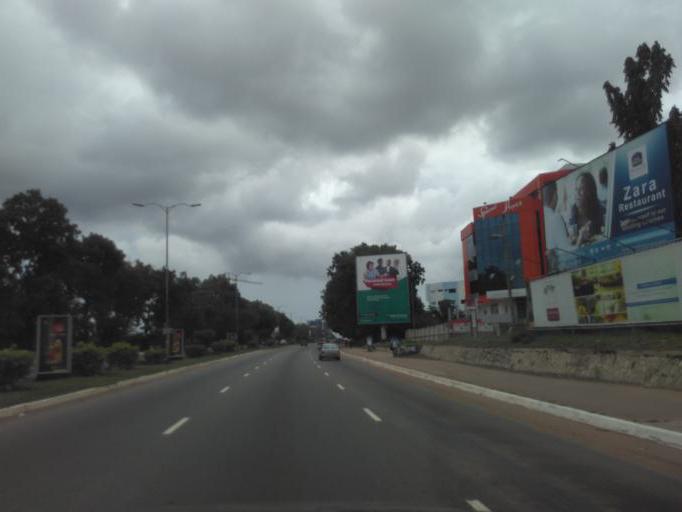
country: GH
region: Greater Accra
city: Medina Estates
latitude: 5.6136
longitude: -0.1761
